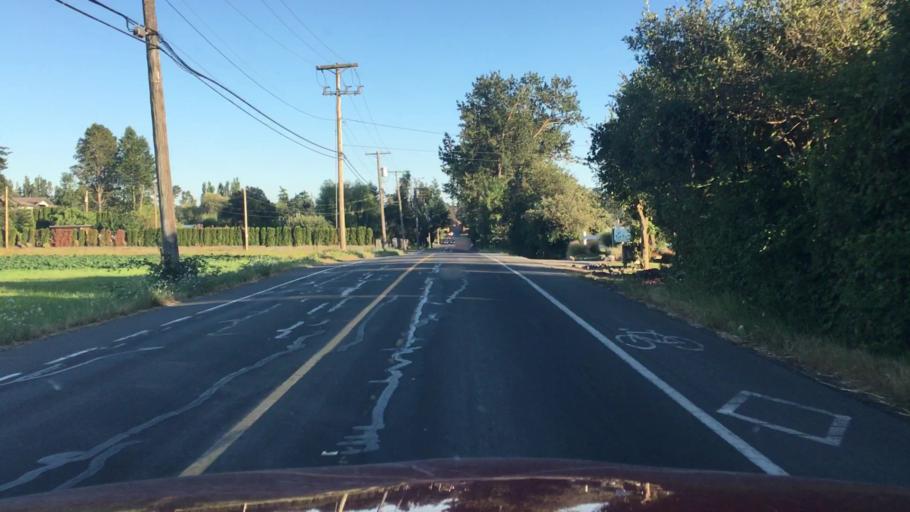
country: CA
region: British Columbia
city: Victoria
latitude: 48.4750
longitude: -123.3521
